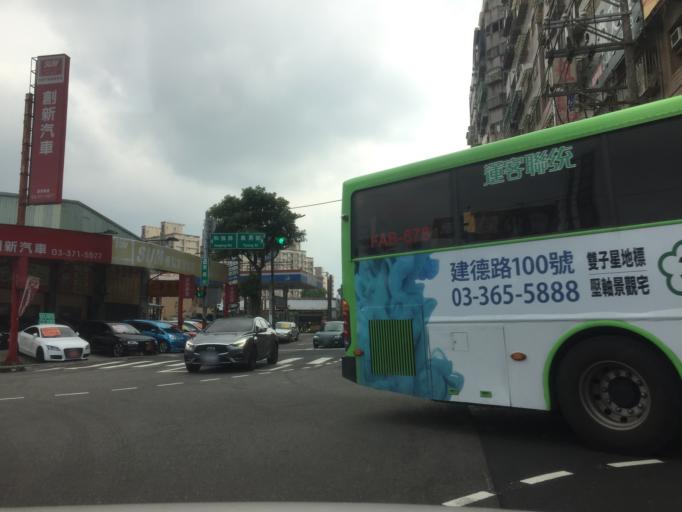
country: TW
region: Taiwan
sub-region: Taoyuan
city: Taoyuan
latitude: 24.9633
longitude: 121.3068
